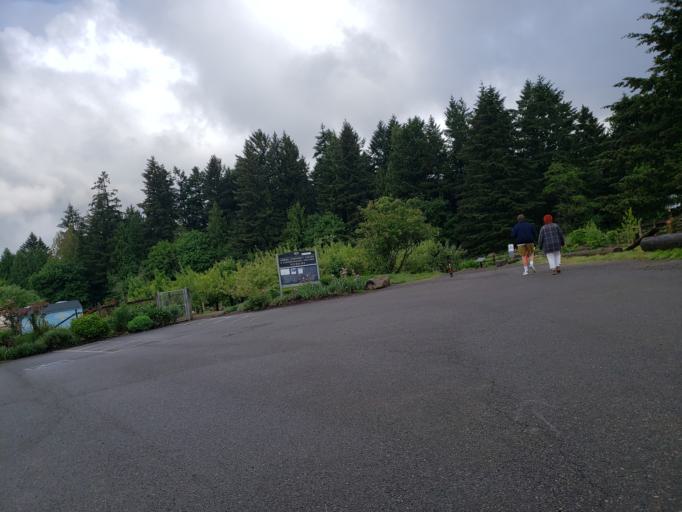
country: US
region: Oregon
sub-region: Washington County
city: Garden Home-Whitford
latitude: 45.4704
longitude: -122.7196
